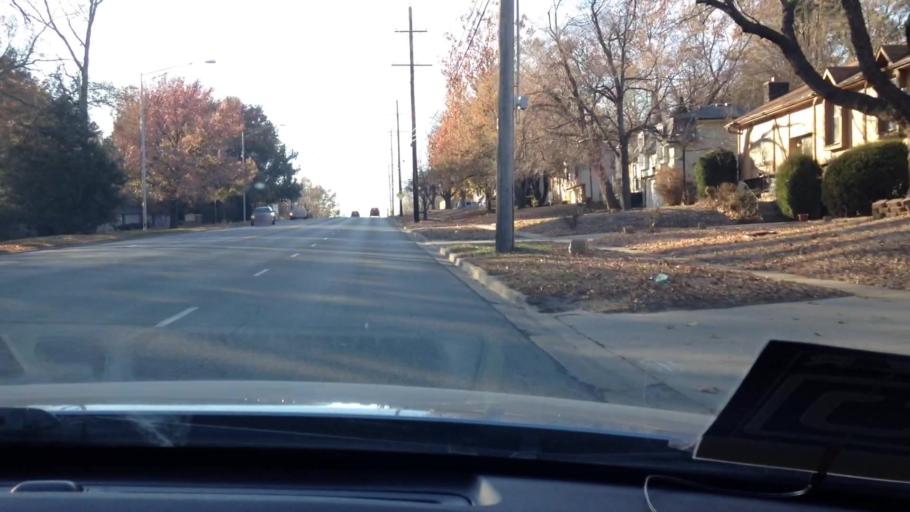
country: US
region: Kansas
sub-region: Johnson County
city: Overland Park
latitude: 38.9568
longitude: -94.6538
